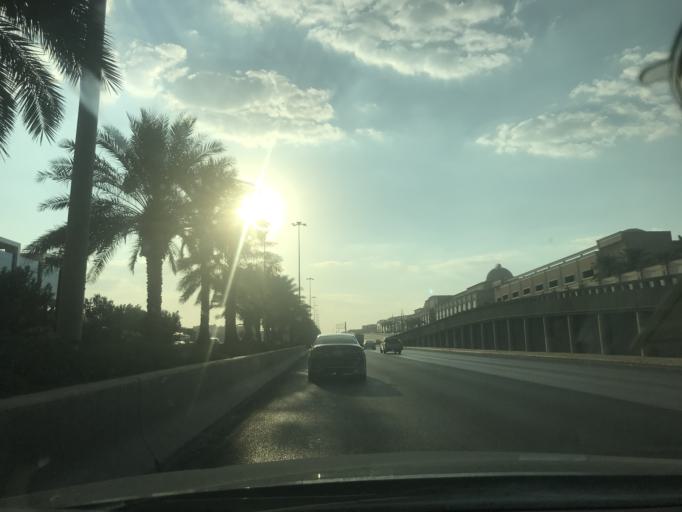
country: SA
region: Ar Riyad
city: Riyadh
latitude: 24.7474
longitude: 46.6148
